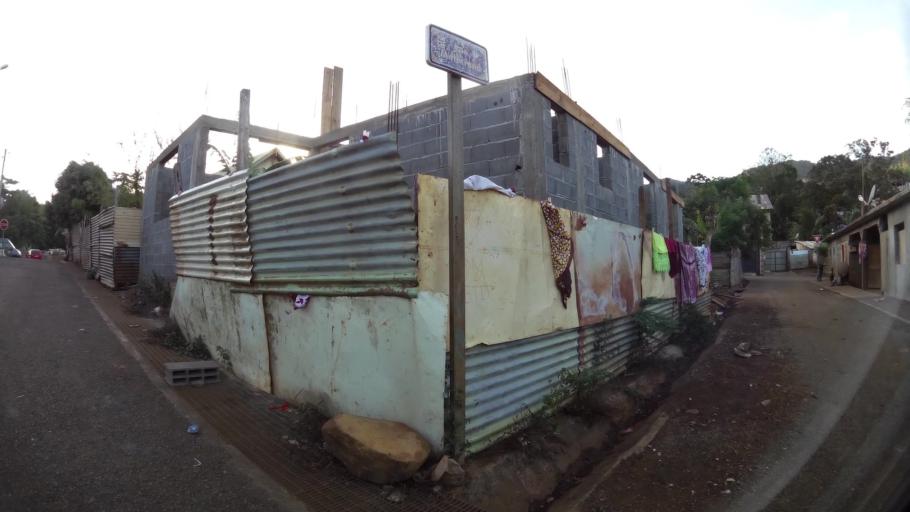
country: YT
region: Dembeni
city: Dembeni
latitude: -12.8360
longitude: 45.1717
